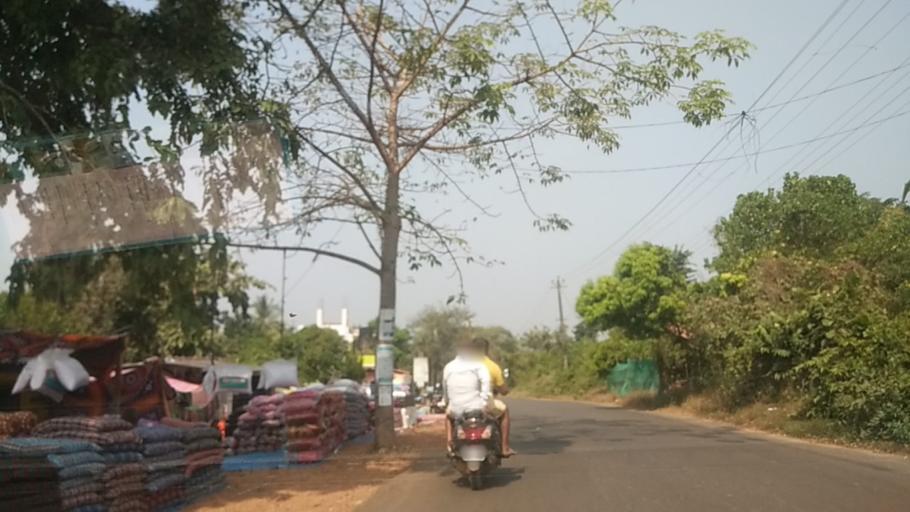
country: IN
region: Goa
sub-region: North Goa
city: Arambol
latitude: 15.6789
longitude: 73.7110
